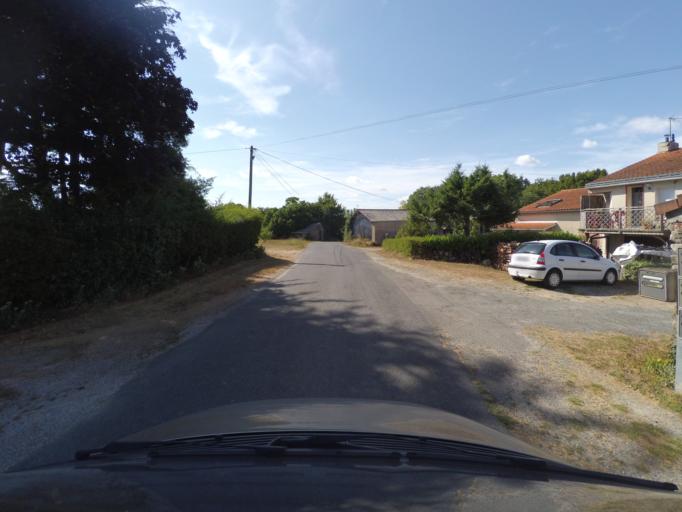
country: FR
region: Pays de la Loire
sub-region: Departement de la Loire-Atlantique
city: Le Bignon
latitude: 47.0912
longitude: -1.4716
